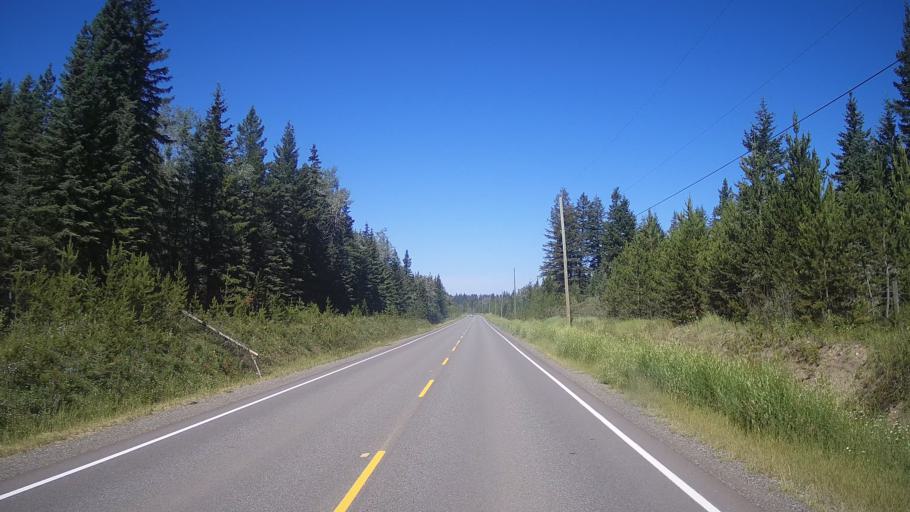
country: CA
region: British Columbia
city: Cache Creek
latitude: 51.5440
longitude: -121.0637
